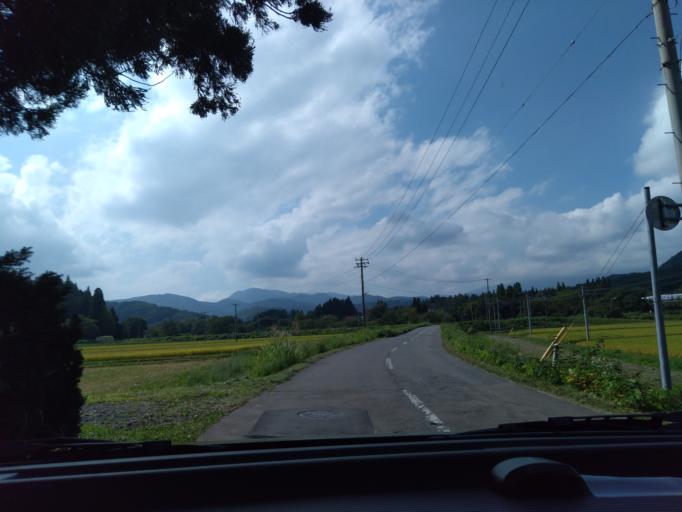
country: JP
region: Iwate
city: Shizukuishi
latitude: 39.6833
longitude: 140.9140
